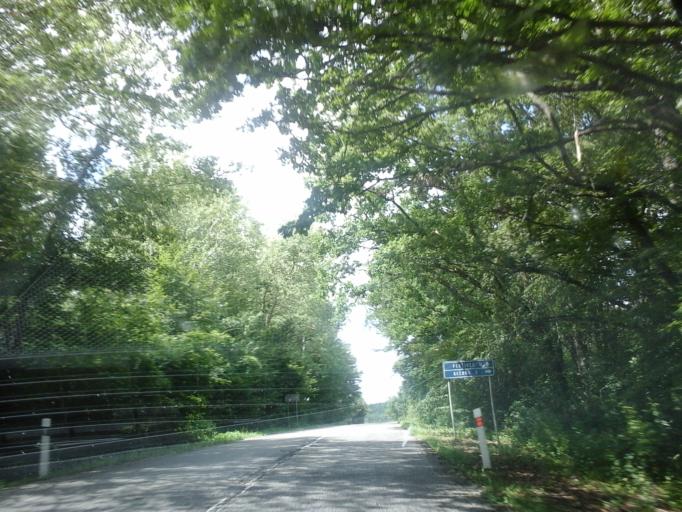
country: HU
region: Borsod-Abauj-Zemplen
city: Putnok
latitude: 48.4748
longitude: 20.4767
